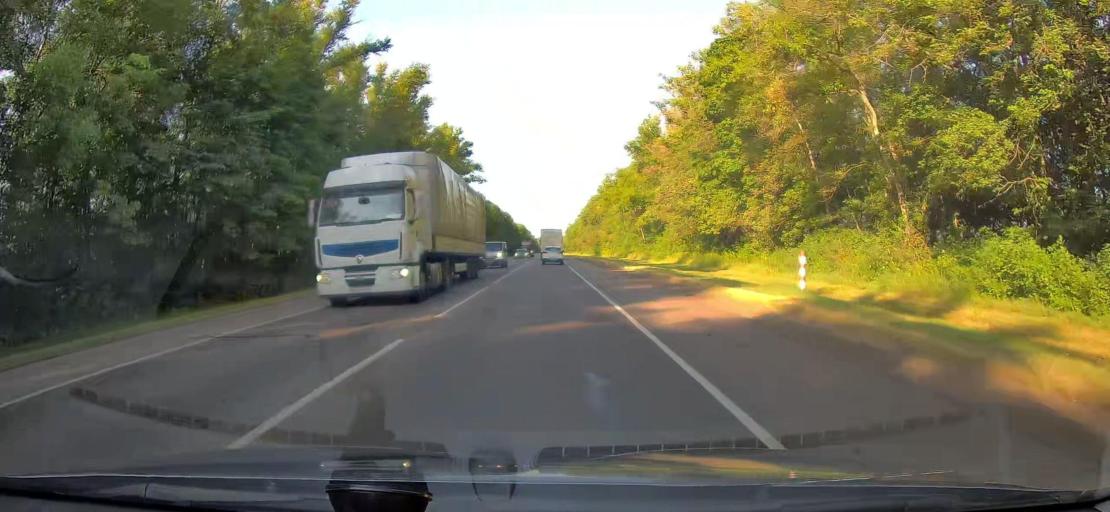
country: RU
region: Tula
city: Chern'
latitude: 53.4754
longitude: 36.9764
